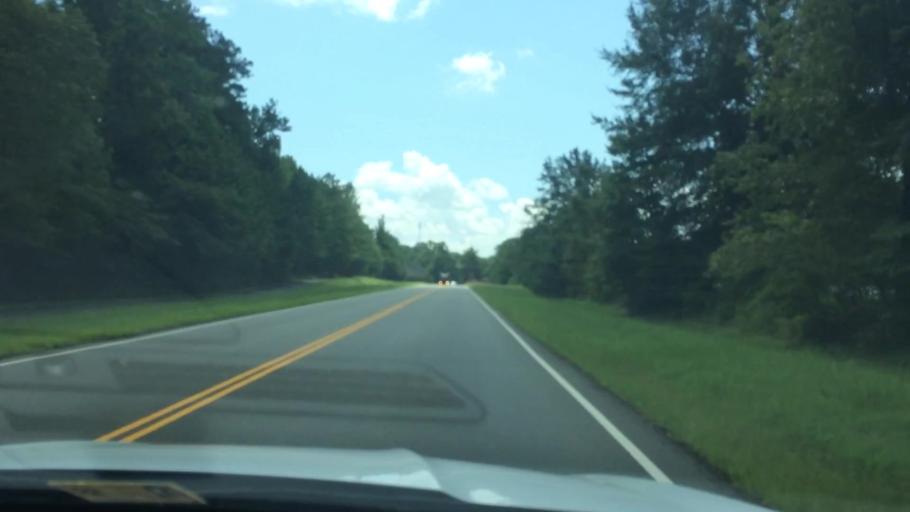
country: US
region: Virginia
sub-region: James City County
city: Williamsburg
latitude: 37.2935
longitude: -76.7344
